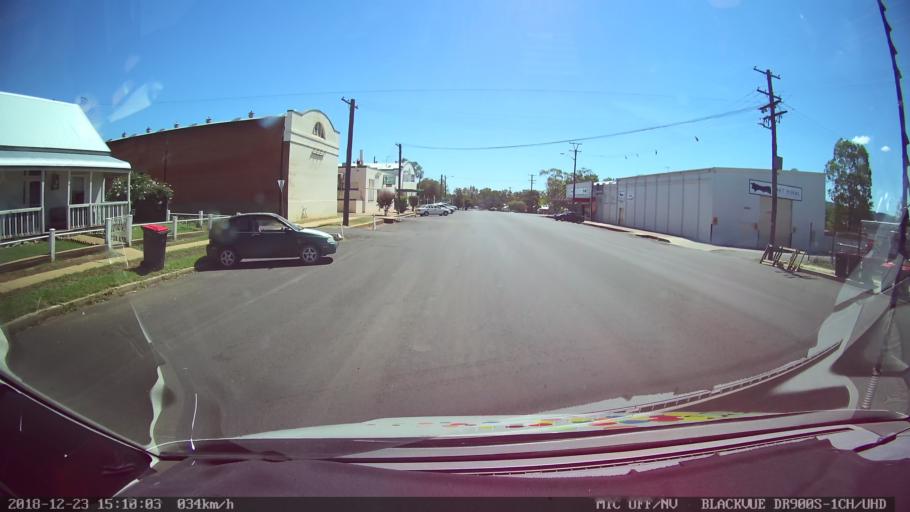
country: AU
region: New South Wales
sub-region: Tamworth Municipality
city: Manilla
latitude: -30.7494
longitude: 150.7222
